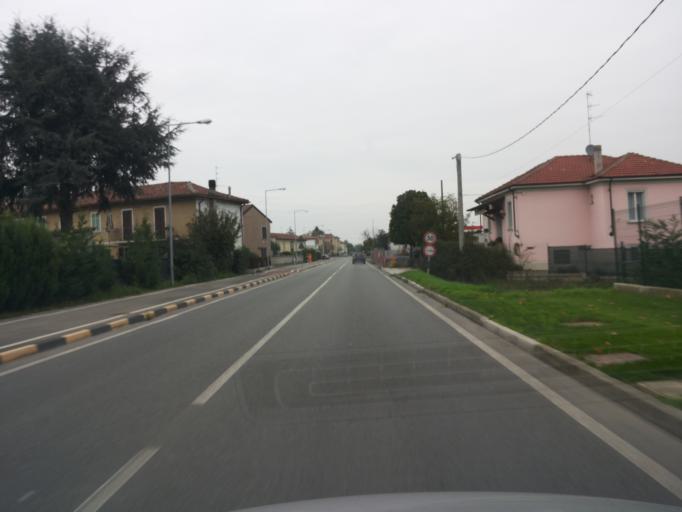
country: IT
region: Piedmont
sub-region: Provincia di Alessandria
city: Terruggia
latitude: 45.1018
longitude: 8.4527
